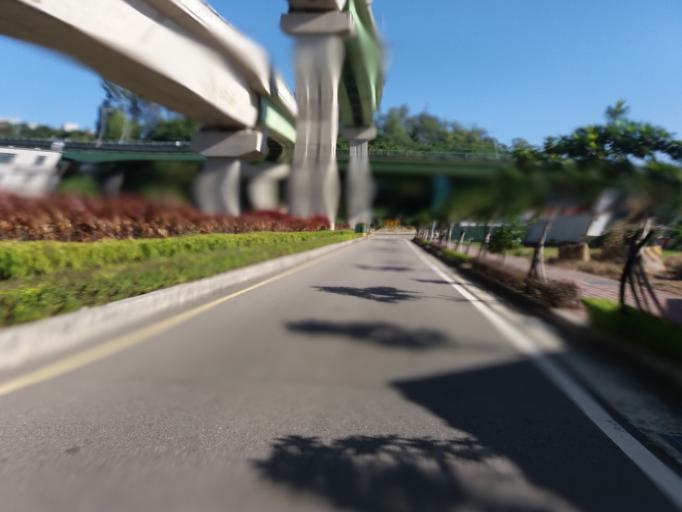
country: TW
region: Taiwan
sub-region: Hsinchu
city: Hsinchu
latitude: 24.7024
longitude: 120.9180
